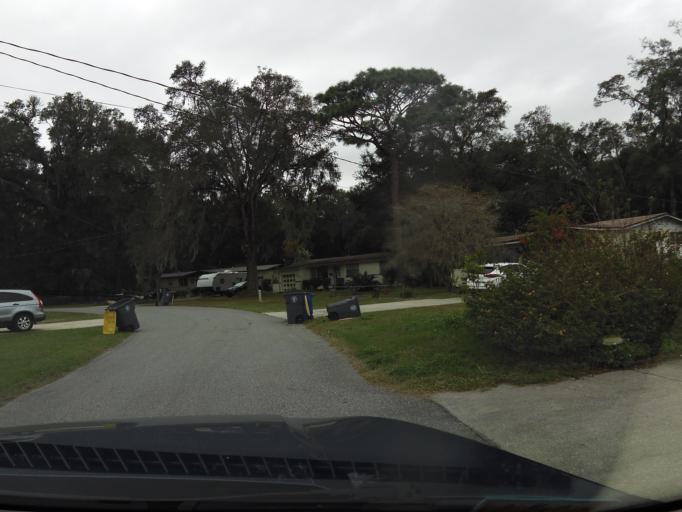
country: US
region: Florida
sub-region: Duval County
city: Jacksonville
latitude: 30.3091
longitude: -81.6044
